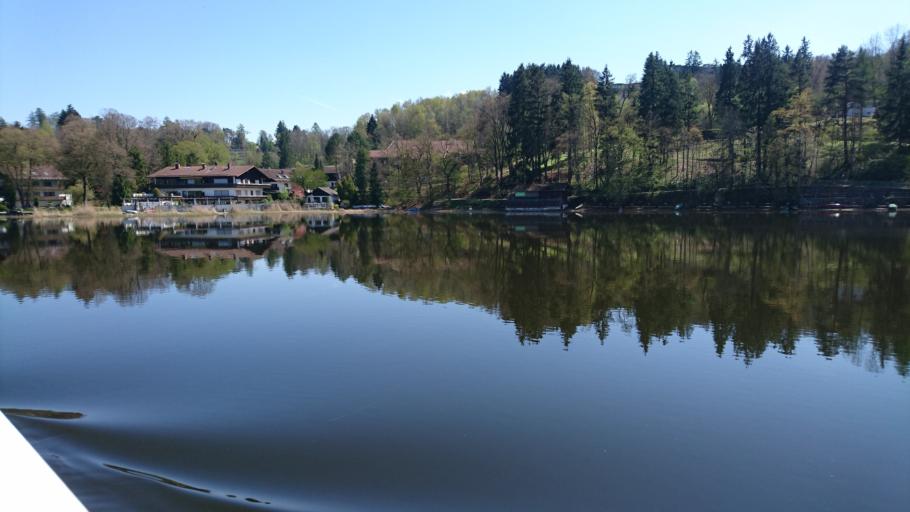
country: DE
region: Bavaria
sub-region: Upper Bavaria
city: Seehausen am Staffelsee
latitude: 47.6800
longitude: 11.1844
